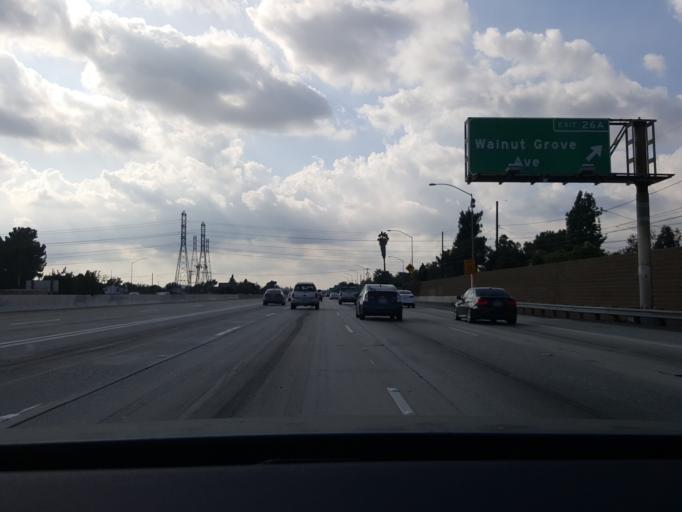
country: US
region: California
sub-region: Los Angeles County
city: Rosemead
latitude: 34.0723
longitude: -118.0803
